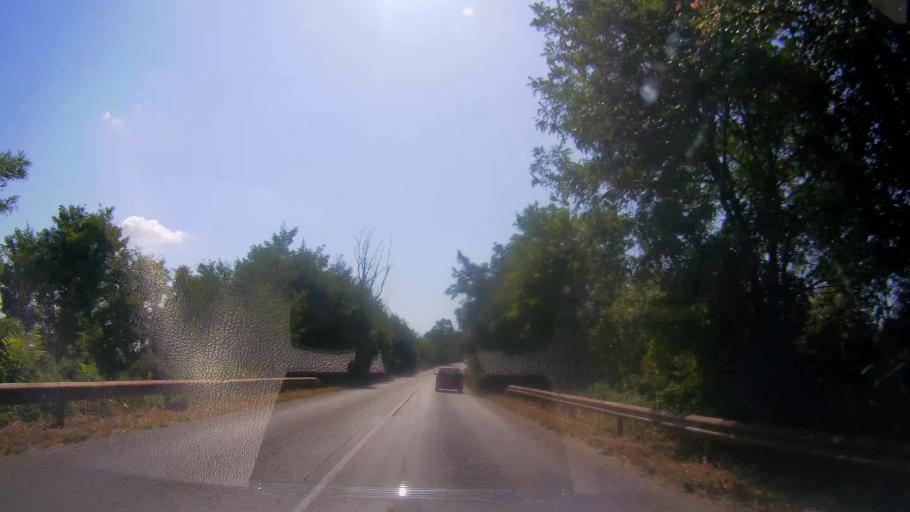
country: BG
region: Veliko Turnovo
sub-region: Obshtina Gorna Oryakhovitsa
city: Purvomaytsi
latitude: 43.2502
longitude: 25.6441
